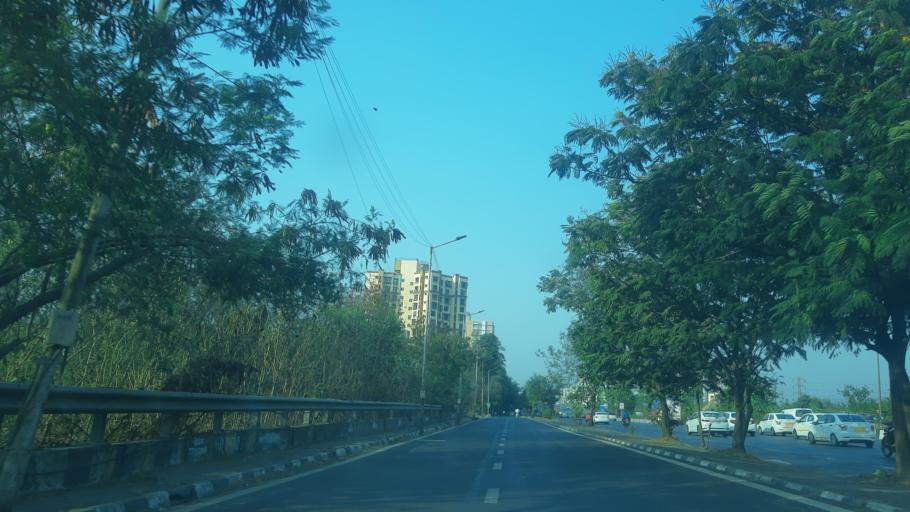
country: IN
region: Maharashtra
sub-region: Thane
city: Thane
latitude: 19.1618
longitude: 72.9613
